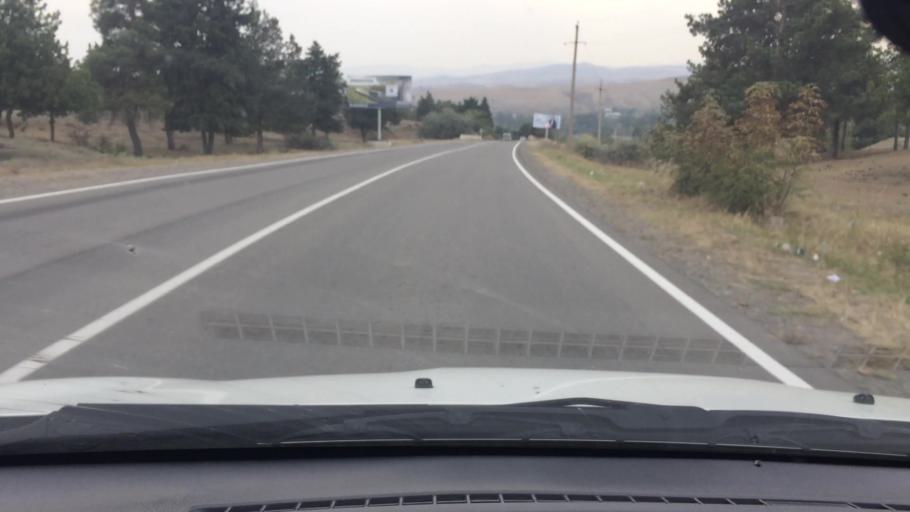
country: GE
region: Kvemo Kartli
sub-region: Gardabani
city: Gardabani
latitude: 41.3475
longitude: 45.0686
